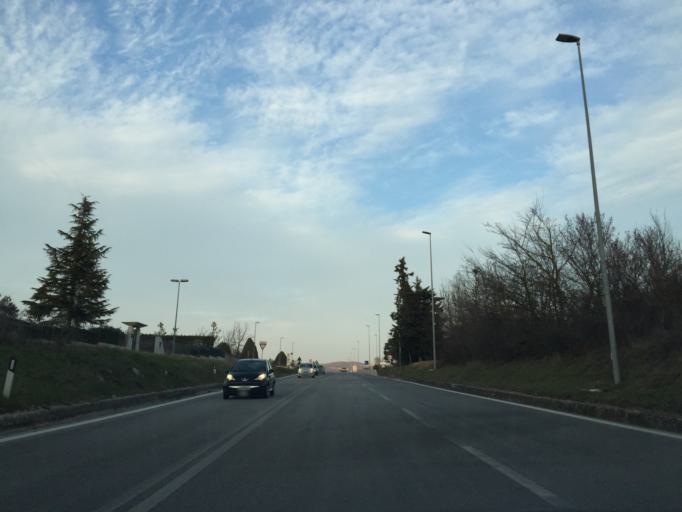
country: IT
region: Molise
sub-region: Provincia di Campobasso
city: Vinchiaturo
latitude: 41.4764
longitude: 14.5722
